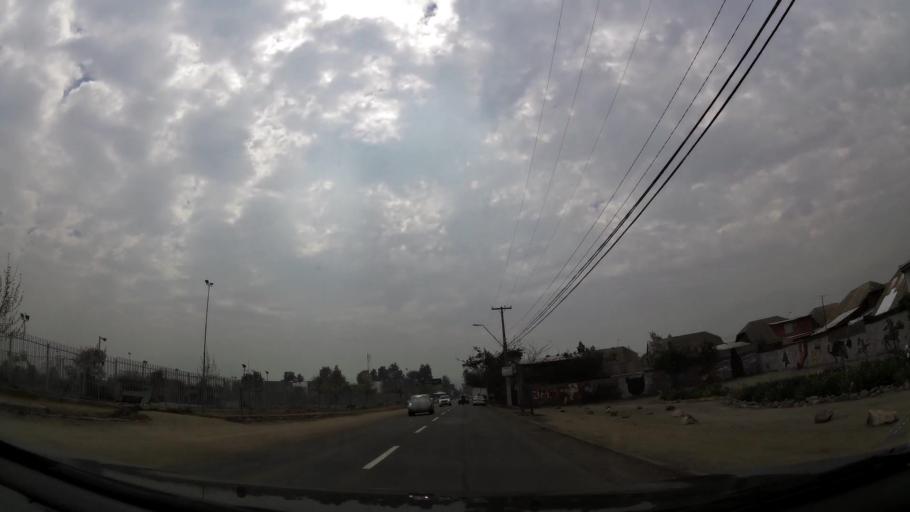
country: CL
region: Santiago Metropolitan
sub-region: Provincia de Chacabuco
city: Chicureo Abajo
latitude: -33.2071
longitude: -70.6841
